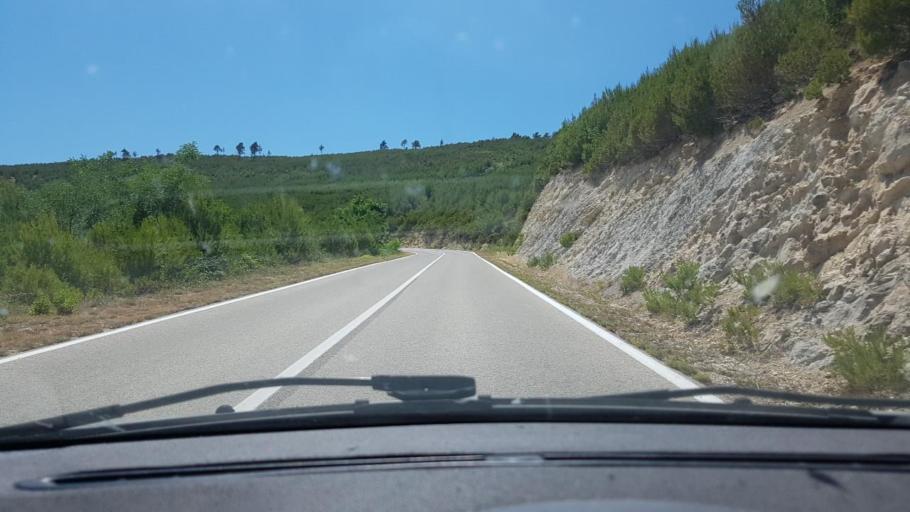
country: HR
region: Sibensko-Kniniska
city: Kistanje
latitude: 43.9042
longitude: 15.9083
